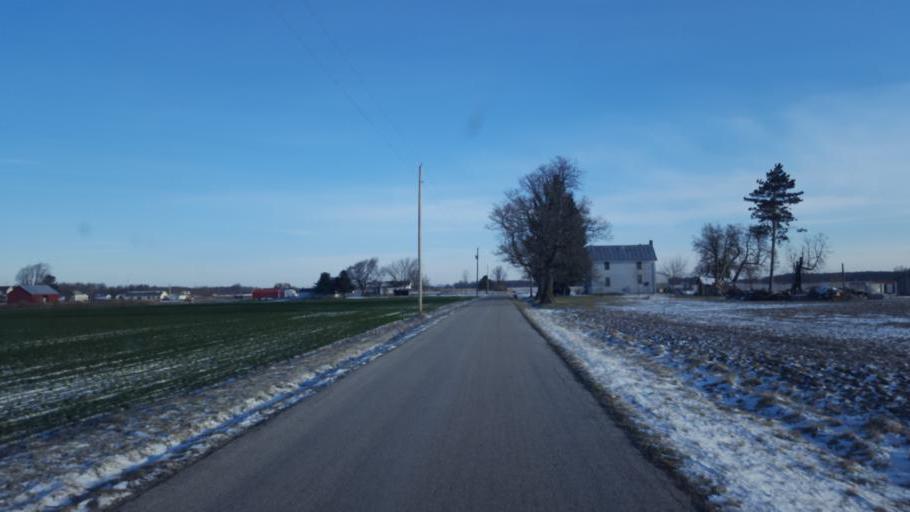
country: US
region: Ohio
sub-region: Morrow County
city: Cardington
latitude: 40.5547
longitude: -82.9337
